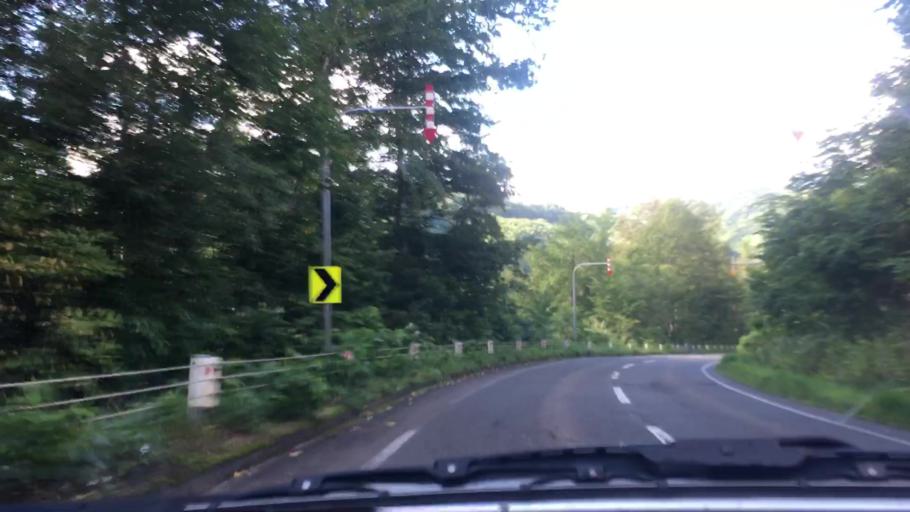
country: JP
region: Hokkaido
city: Otofuke
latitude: 43.1788
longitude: 142.9292
